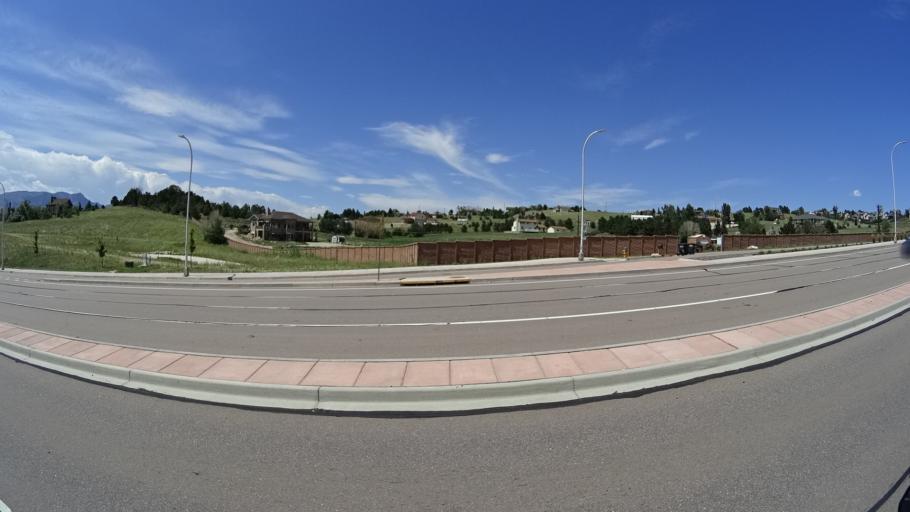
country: US
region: Colorado
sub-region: El Paso County
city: Cimarron Hills
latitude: 38.9339
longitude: -104.7681
